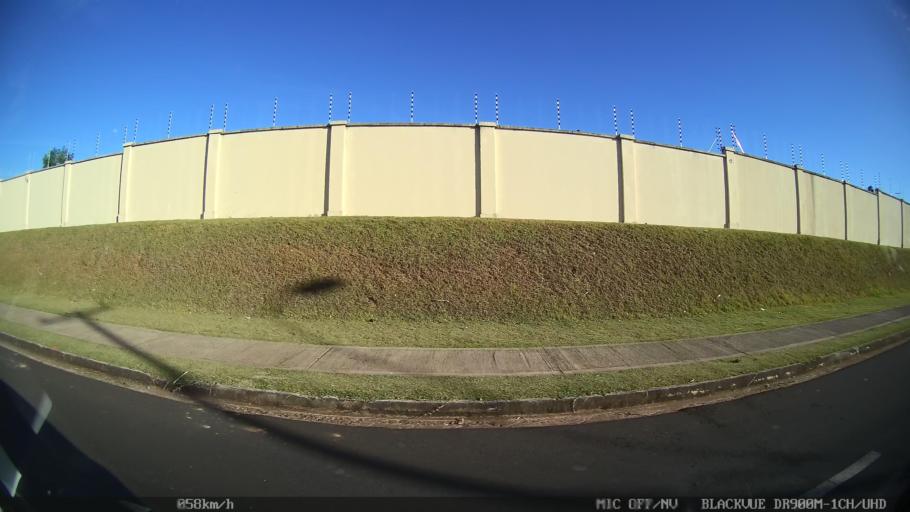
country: BR
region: Sao Paulo
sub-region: Franca
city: Franca
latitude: -20.5780
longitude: -47.4110
